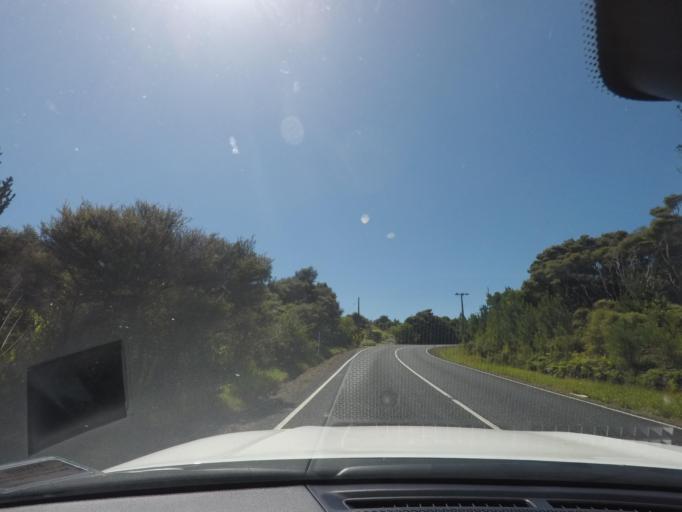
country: NZ
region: Auckland
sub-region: Auckland
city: Parakai
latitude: -36.5839
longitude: 174.3308
